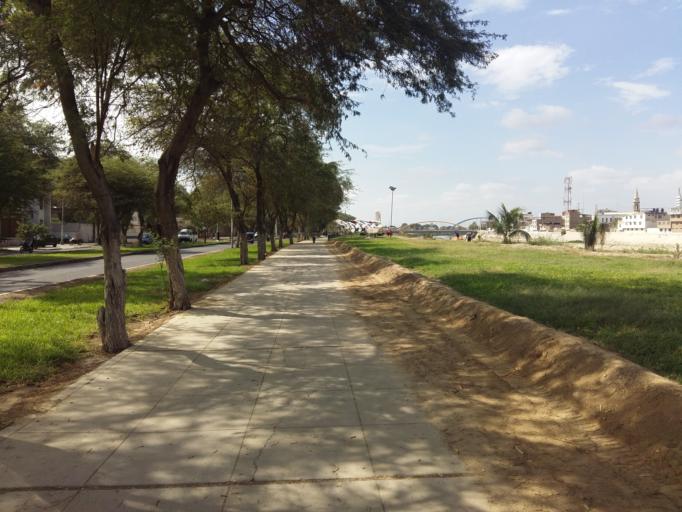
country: PE
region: Piura
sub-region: Provincia de Piura
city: Piura
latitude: -5.1891
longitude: -80.6236
